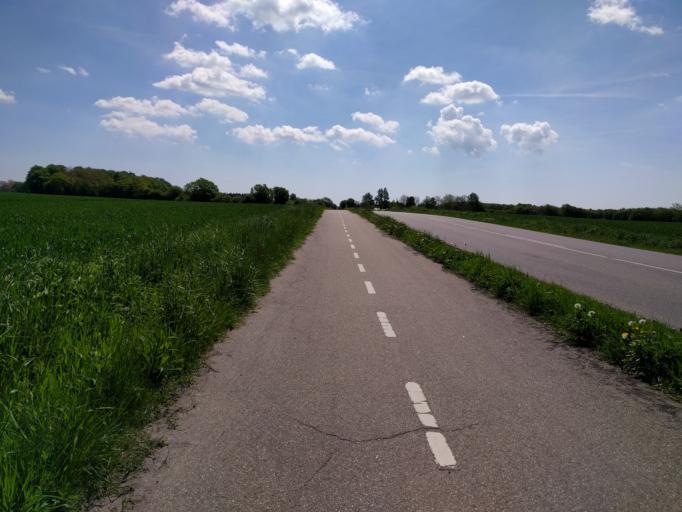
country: DK
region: Zealand
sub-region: Guldborgsund Kommune
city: Nykobing Falster
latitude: 54.7540
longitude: 11.9312
